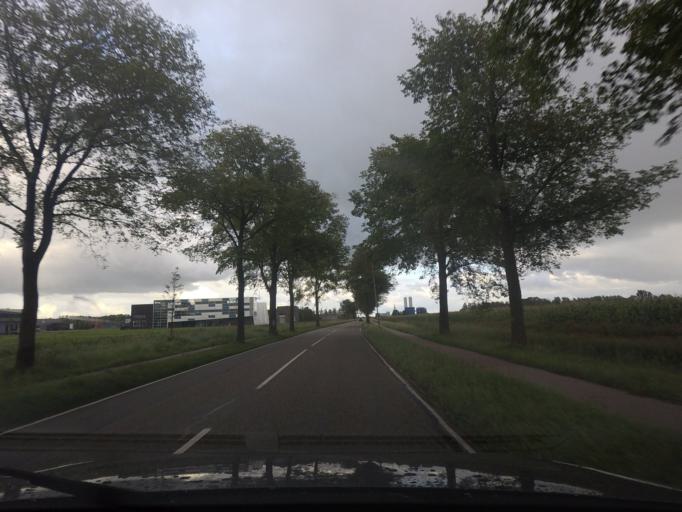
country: NL
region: North Holland
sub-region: Gemeente Alkmaar
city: Alkmaar
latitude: 52.5903
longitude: 4.7452
